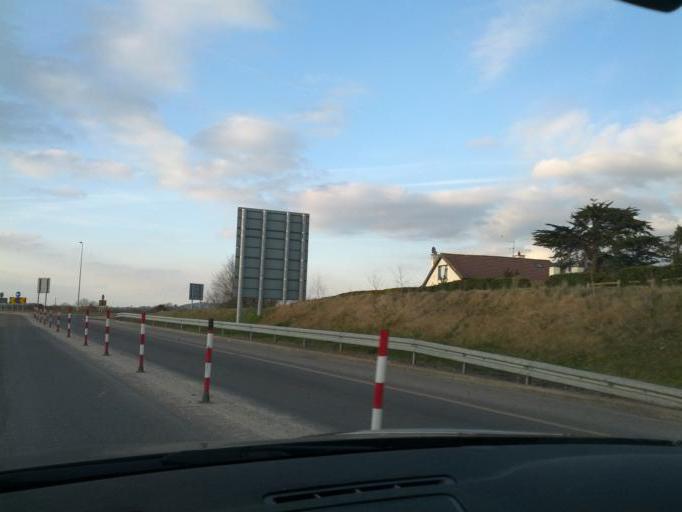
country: IE
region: Munster
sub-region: North Tipperary
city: Nenagh
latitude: 52.8602
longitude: -8.1199
